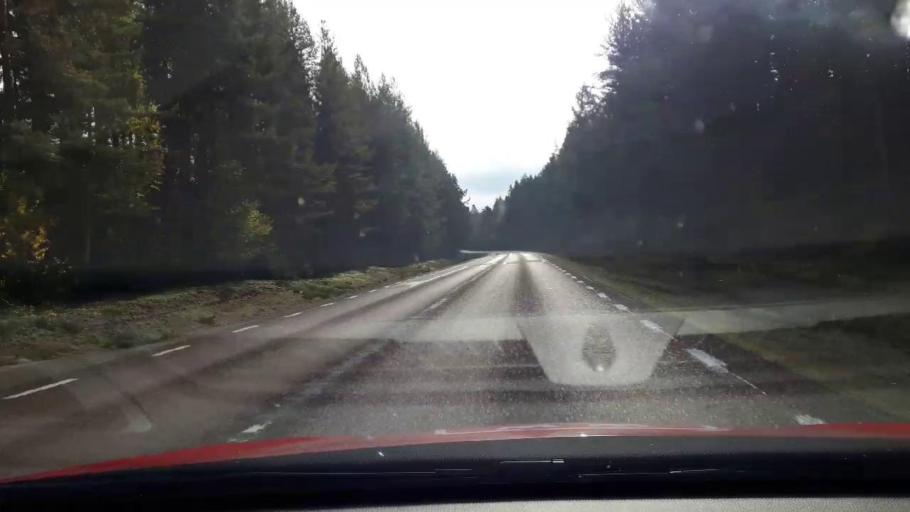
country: SE
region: Gaevleborg
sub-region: Ljusdals Kommun
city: Farila
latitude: 61.8820
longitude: 15.7091
